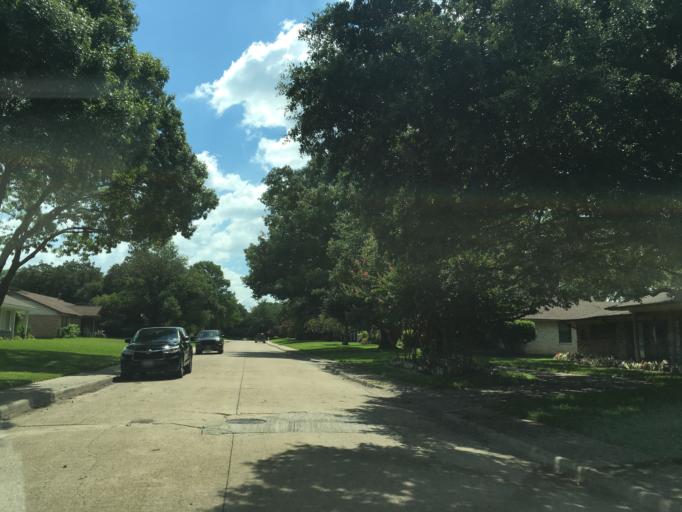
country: US
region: Texas
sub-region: Dallas County
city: Farmers Branch
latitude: 32.9219
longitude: -96.8630
